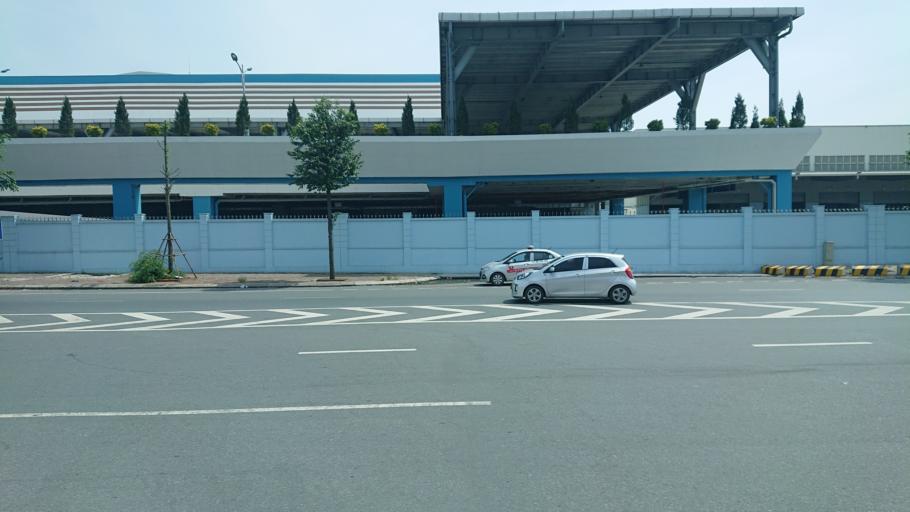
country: VN
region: Ha Noi
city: Soc Son
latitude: 21.2124
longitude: 105.8055
